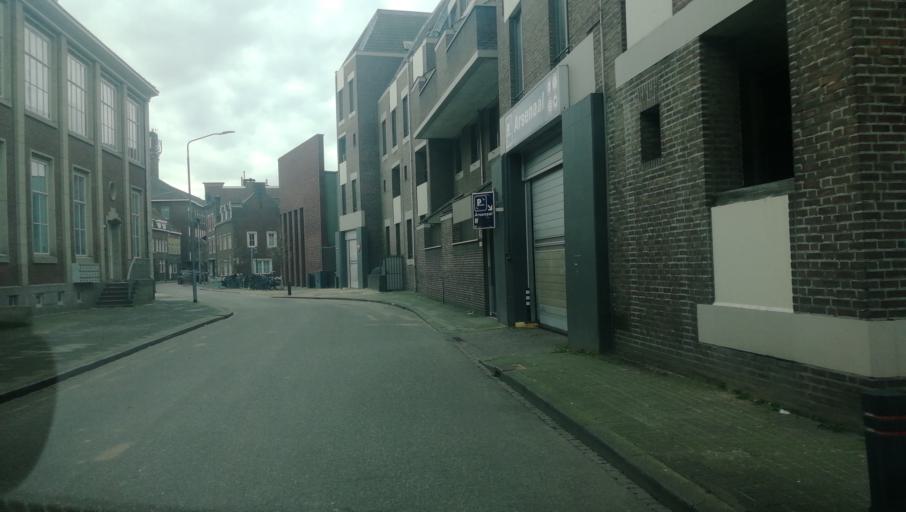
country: NL
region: Limburg
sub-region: Gemeente Venlo
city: Venlo
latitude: 51.3691
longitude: 6.1725
